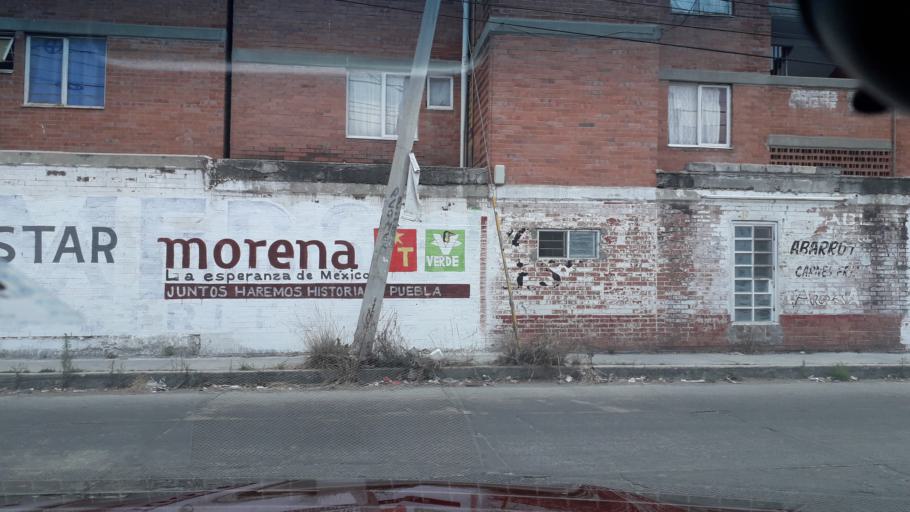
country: MX
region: Puebla
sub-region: Puebla
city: El Capulo (La Quebradora)
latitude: 18.9945
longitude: -98.2419
